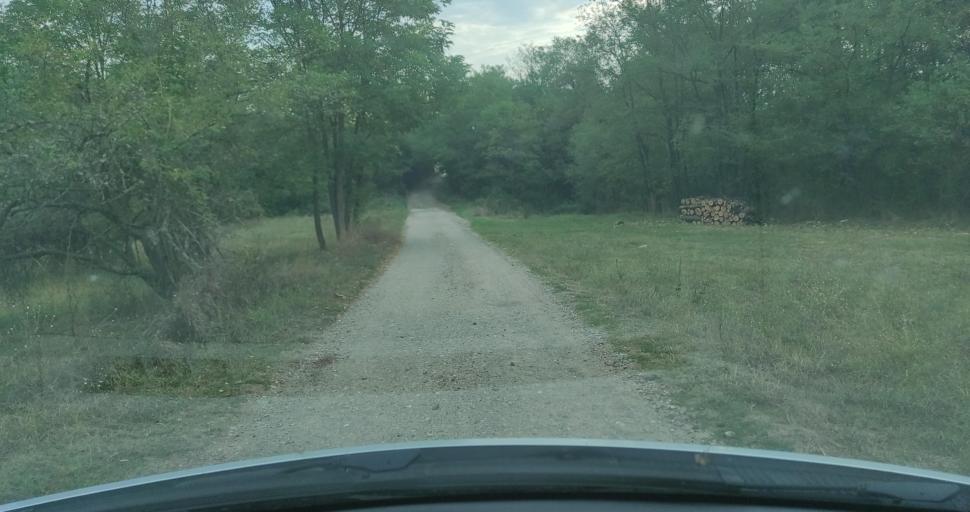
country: RS
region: Central Serbia
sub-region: Pcinjski Okrug
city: Vladicin Han
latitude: 42.6762
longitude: 22.0082
